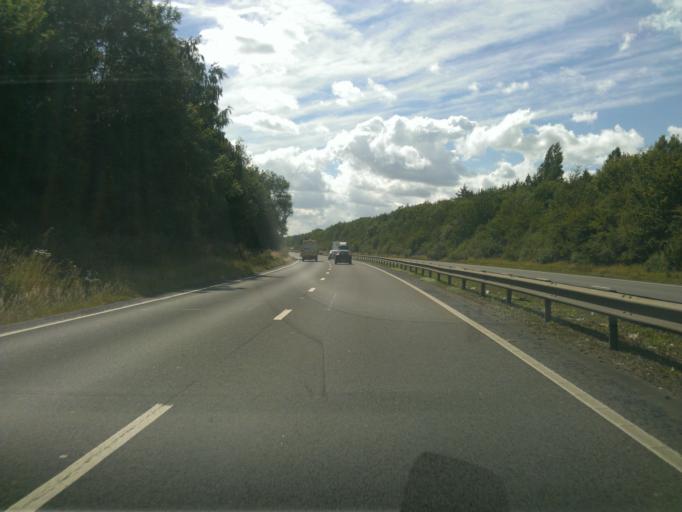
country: GB
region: England
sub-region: Northamptonshire
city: Burton Latimer
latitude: 52.3791
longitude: -0.6673
